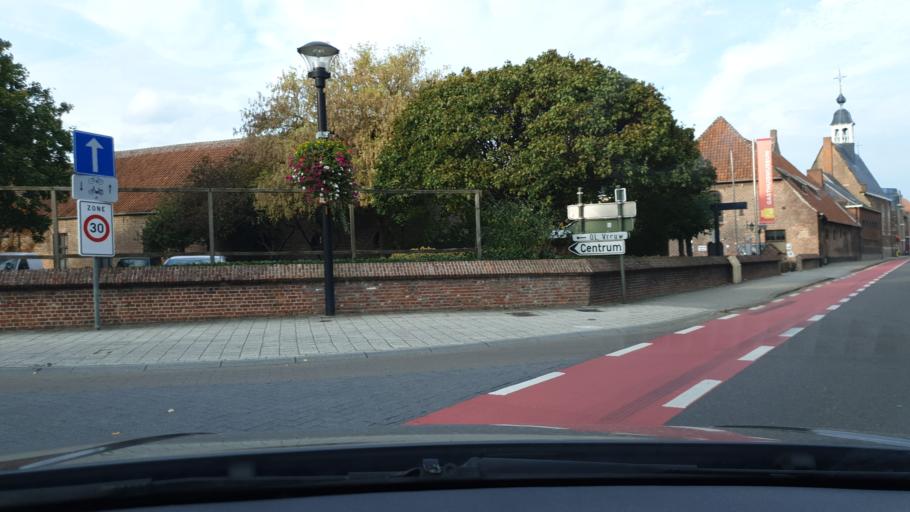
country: BE
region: Flanders
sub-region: Provincie Antwerpen
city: Geel
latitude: 51.1614
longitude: 4.9991
